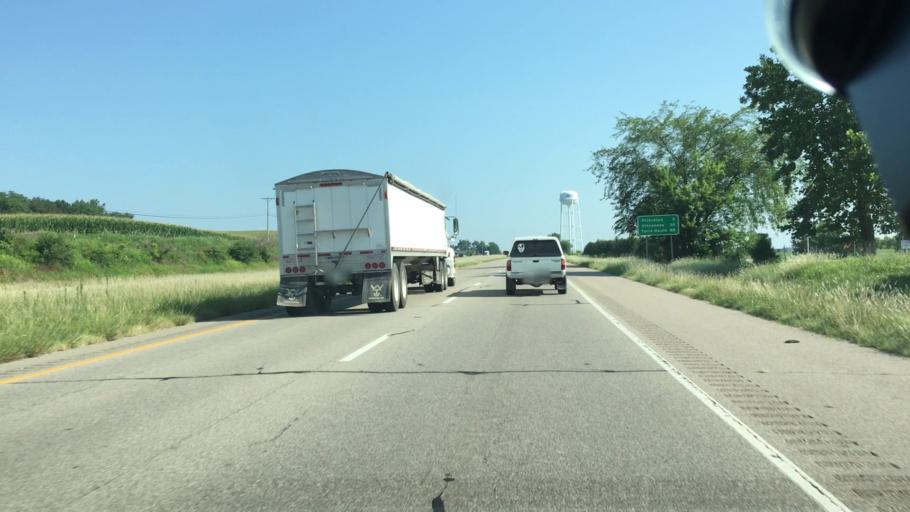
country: US
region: Indiana
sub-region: Gibson County
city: Fort Branch
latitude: 38.2843
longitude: -87.5675
